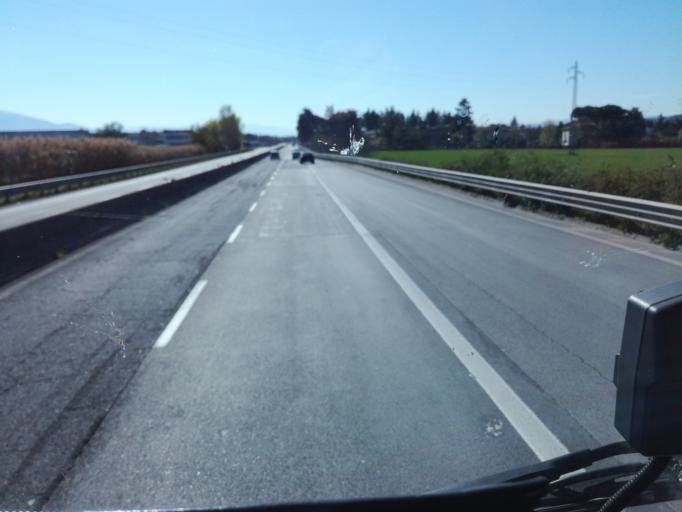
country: IT
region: Umbria
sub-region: Provincia di Perugia
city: Ponte Felcino
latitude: 43.1147
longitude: 12.4540
